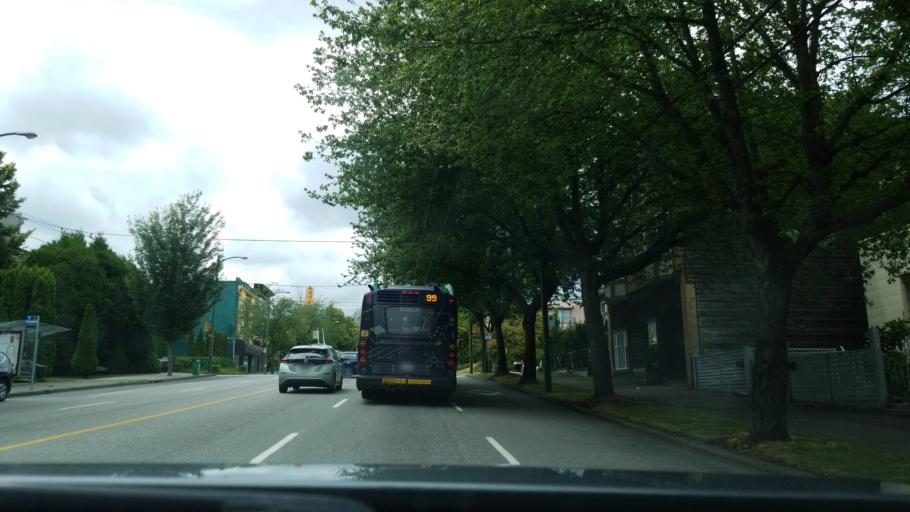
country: CA
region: British Columbia
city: Vancouver
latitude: 49.2625
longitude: -123.0843
